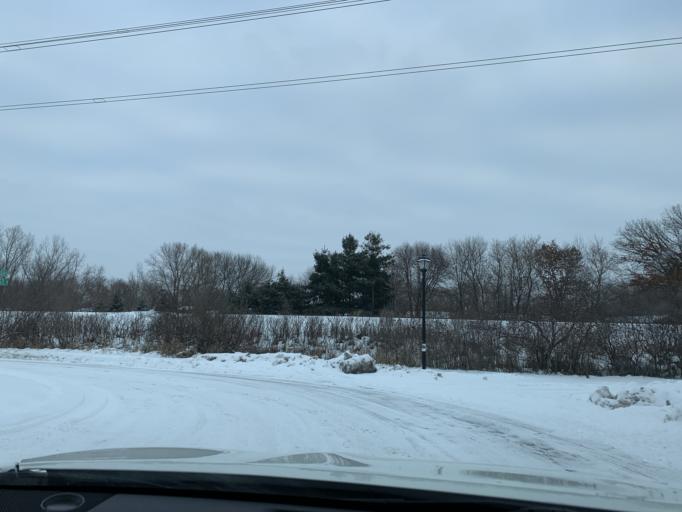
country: US
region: Minnesota
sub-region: Anoka County
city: Coon Rapids
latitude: 45.1595
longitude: -93.2947
